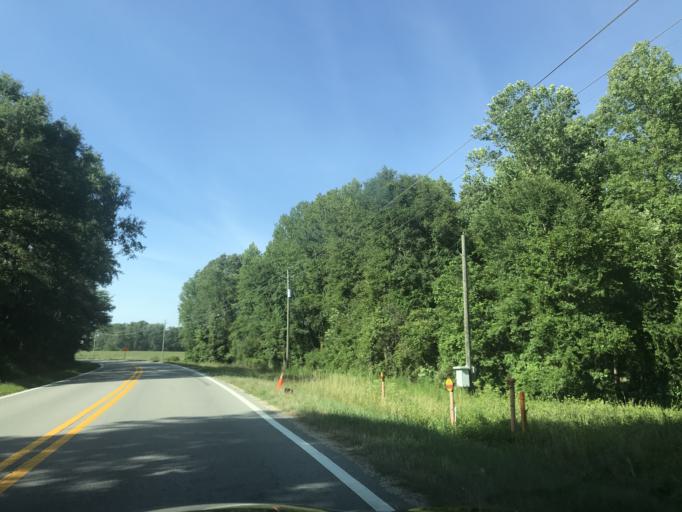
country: US
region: North Carolina
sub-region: Johnston County
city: Clayton
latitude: 35.6042
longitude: -78.5339
